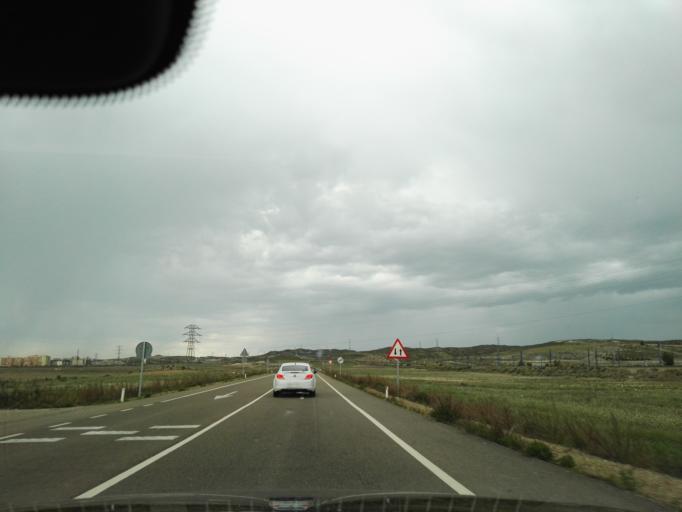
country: ES
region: Aragon
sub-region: Provincia de Zaragoza
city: Montecanal
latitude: 41.6258
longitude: -0.9886
